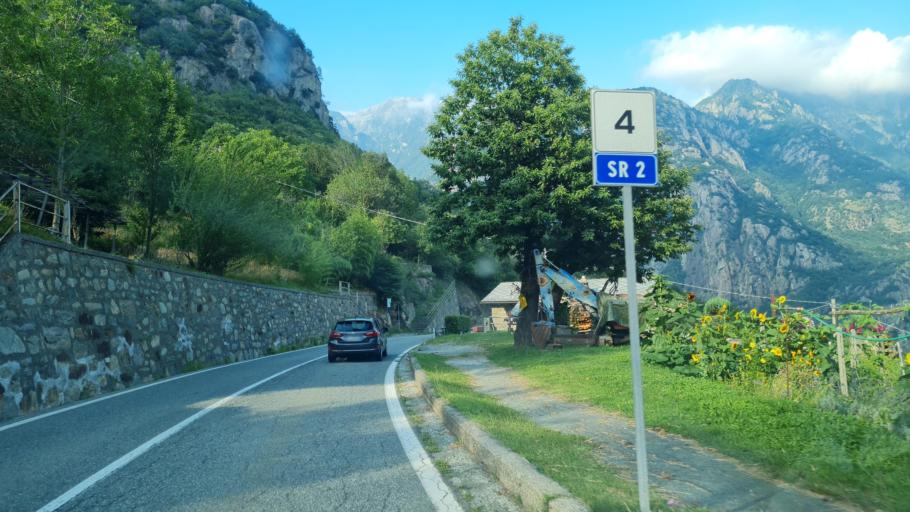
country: IT
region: Aosta Valley
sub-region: Valle d'Aosta
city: Hone
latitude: 45.6125
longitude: 7.7228
